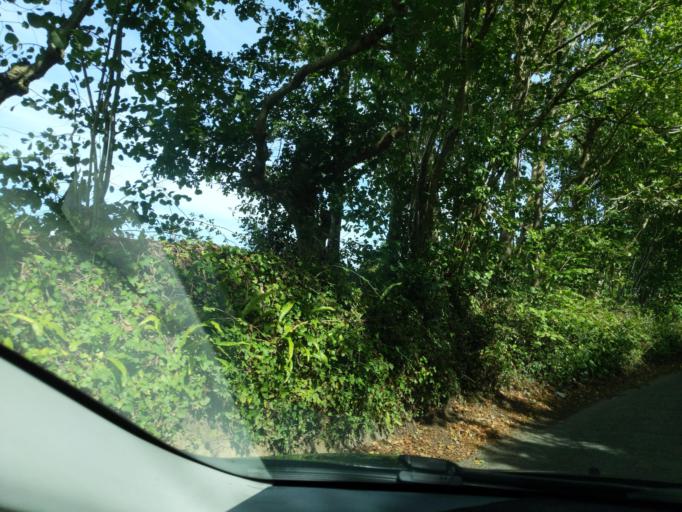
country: GB
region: England
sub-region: Cornwall
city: Torpoint
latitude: 50.3573
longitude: -4.2260
